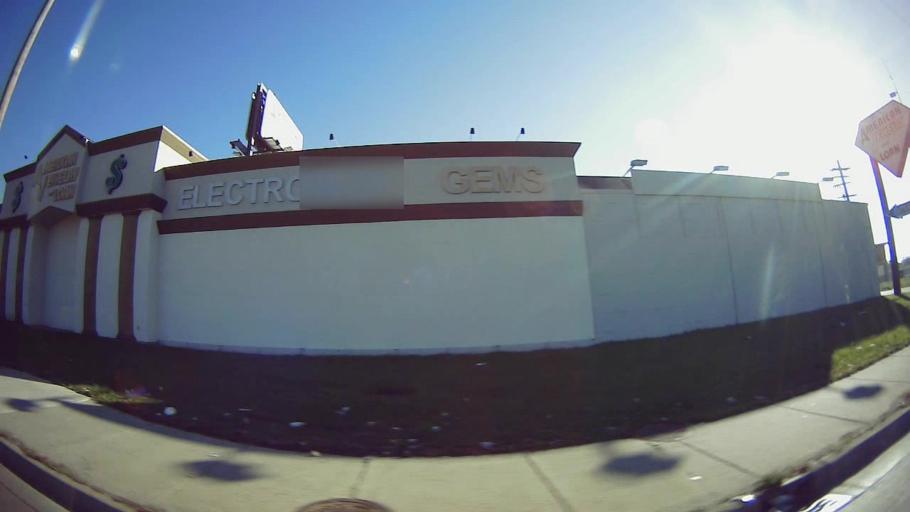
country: US
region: Michigan
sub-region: Oakland County
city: Oak Park
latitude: 42.4433
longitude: -83.2004
